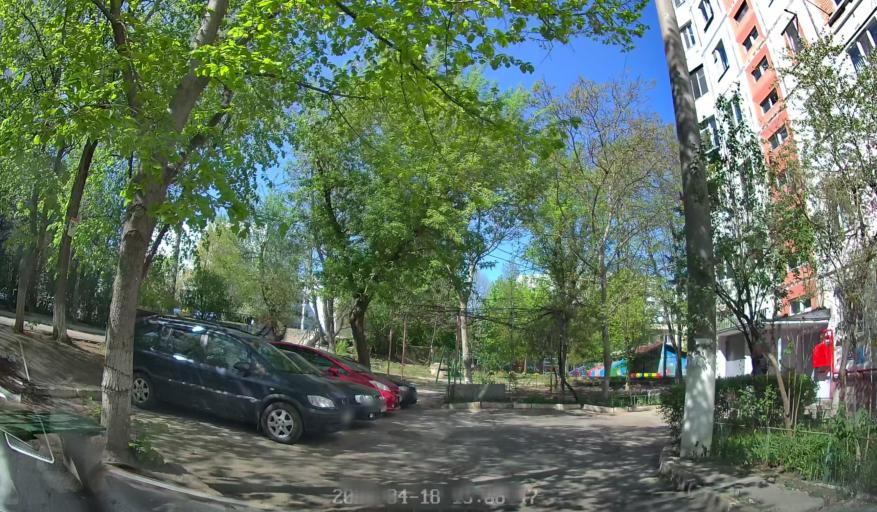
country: MD
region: Chisinau
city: Chisinau
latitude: 47.0447
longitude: 28.8870
